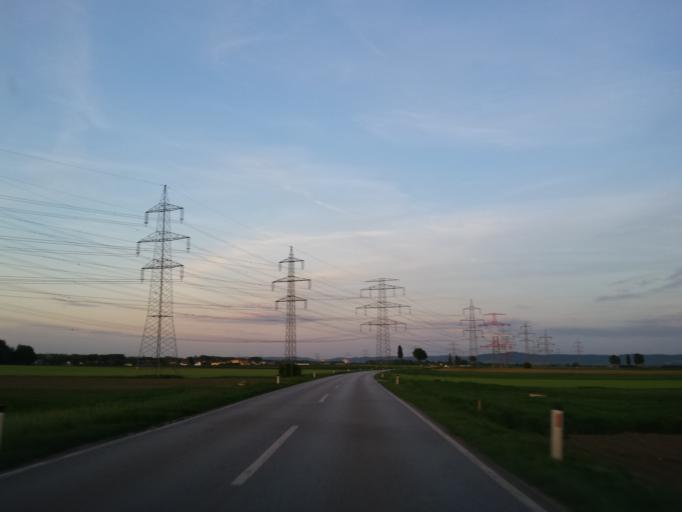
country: AT
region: Lower Austria
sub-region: Politischer Bezirk Tulln
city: Michelhausen
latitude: 48.3280
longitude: 15.9593
